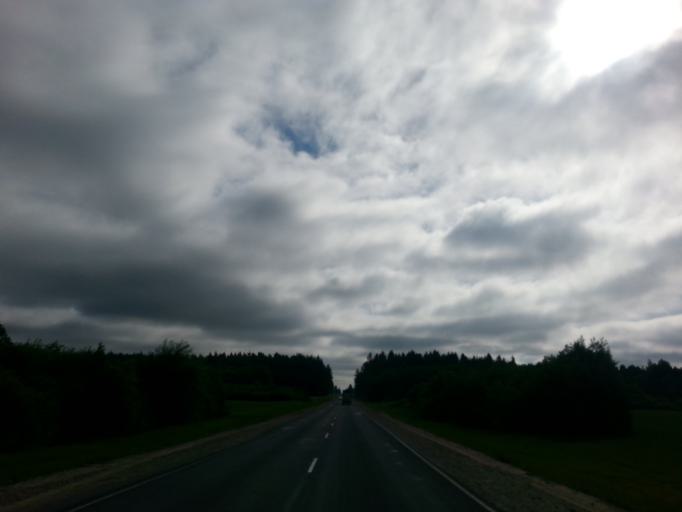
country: BY
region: Vitebsk
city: Mosar
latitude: 55.0776
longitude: 27.4338
